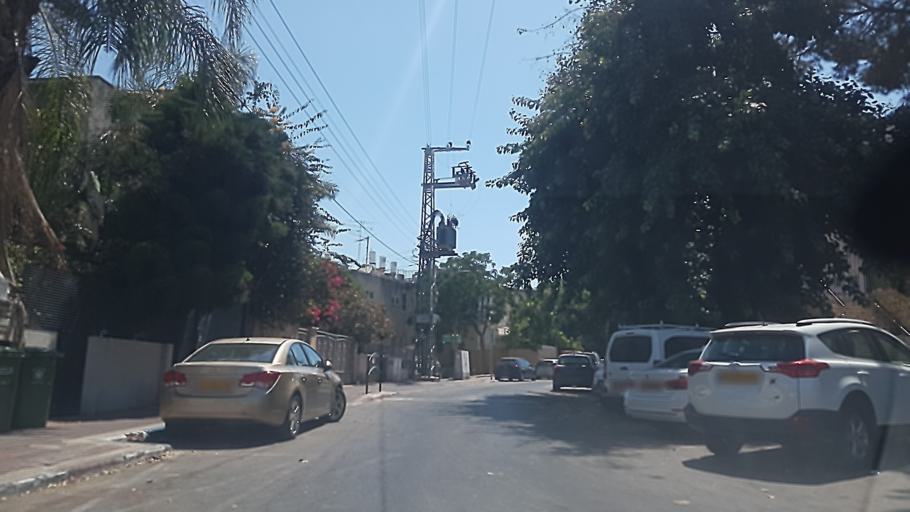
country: IL
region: Tel Aviv
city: Bene Beraq
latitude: 32.0805
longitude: 34.8246
